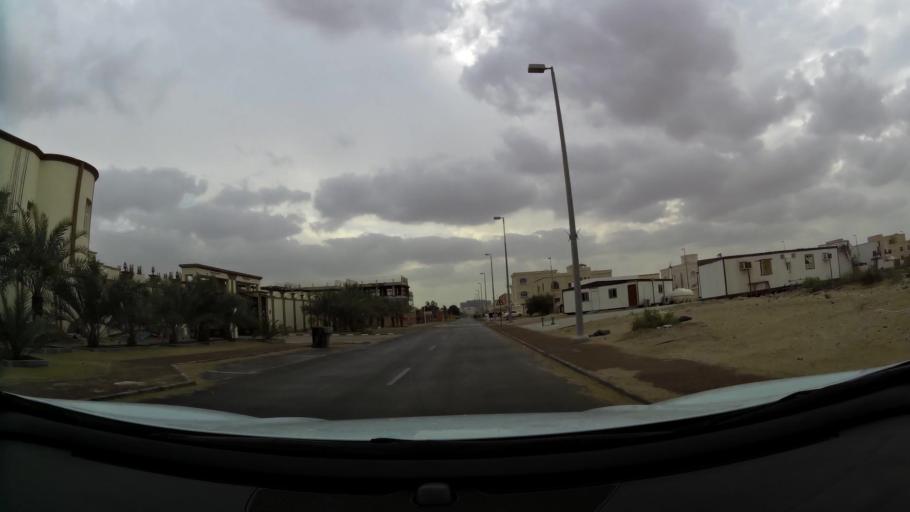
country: AE
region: Abu Dhabi
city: Abu Dhabi
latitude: 24.3474
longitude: 54.6330
